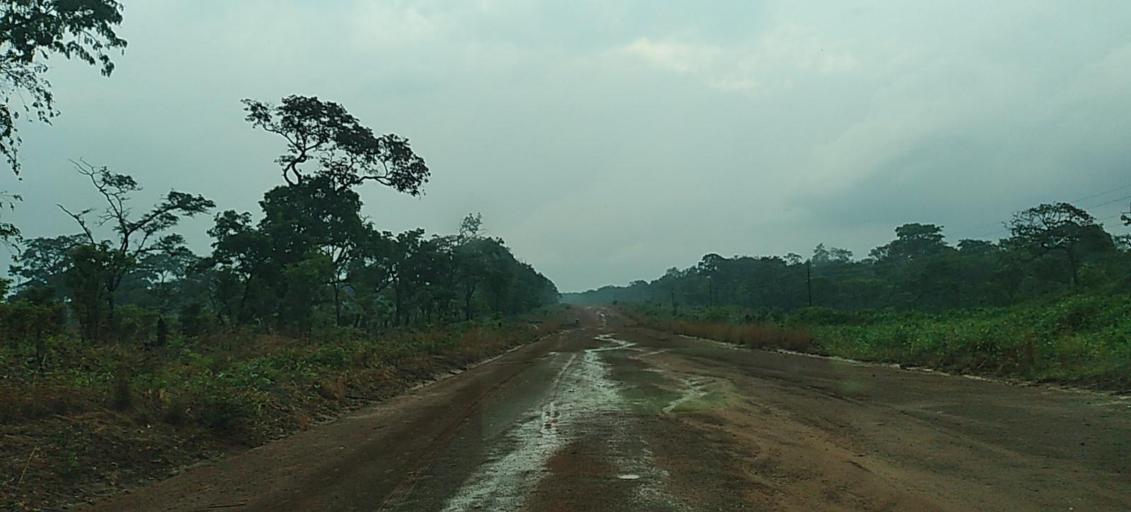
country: ZM
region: North-Western
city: Mwinilunga
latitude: -11.5769
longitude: 24.3925
